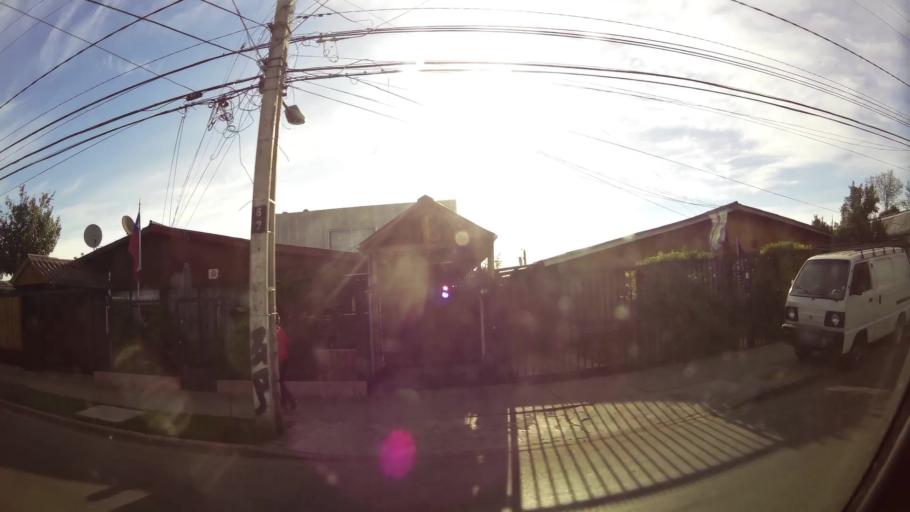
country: CL
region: Santiago Metropolitan
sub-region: Provincia de Santiago
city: Lo Prado
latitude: -33.4723
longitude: -70.6991
